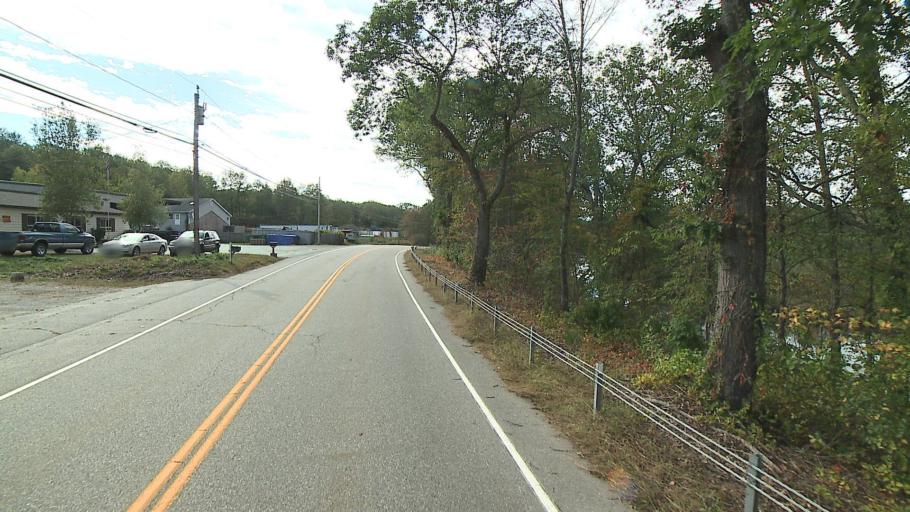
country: US
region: Connecticut
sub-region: Windham County
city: Thompson
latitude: 41.9534
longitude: -71.8844
